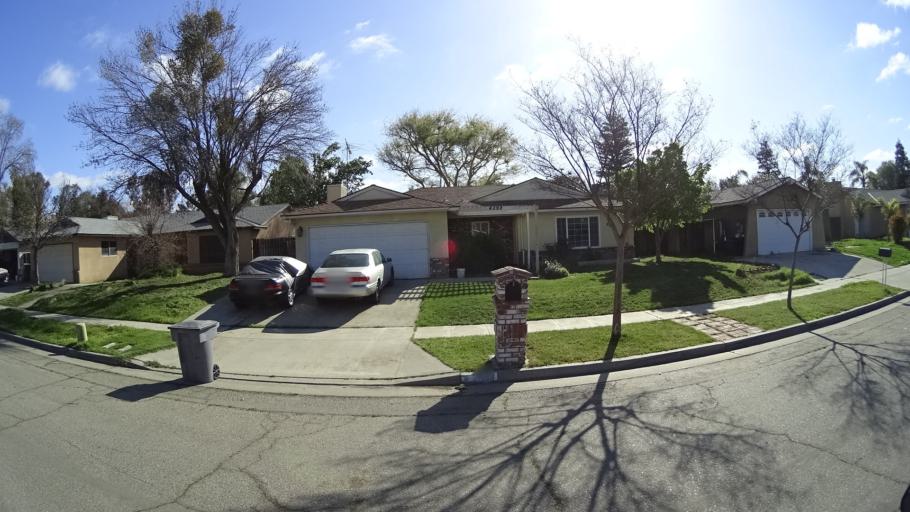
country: US
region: California
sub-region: Fresno County
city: West Park
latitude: 36.7993
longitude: -119.8764
